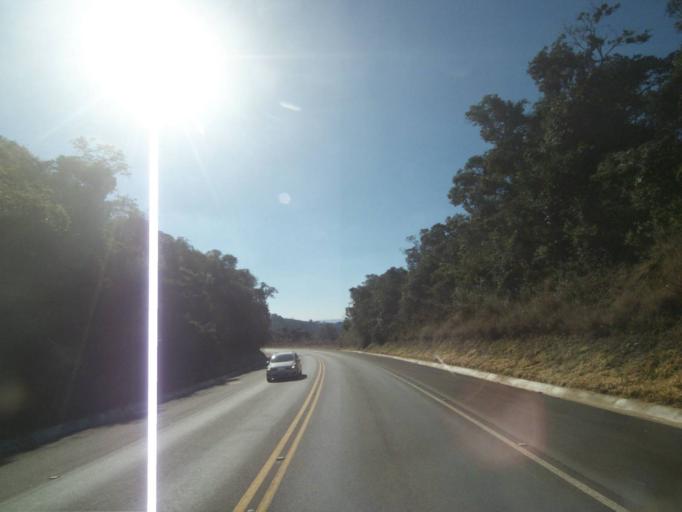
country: BR
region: Parana
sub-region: Tibagi
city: Tibagi
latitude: -24.7772
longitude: -50.4615
